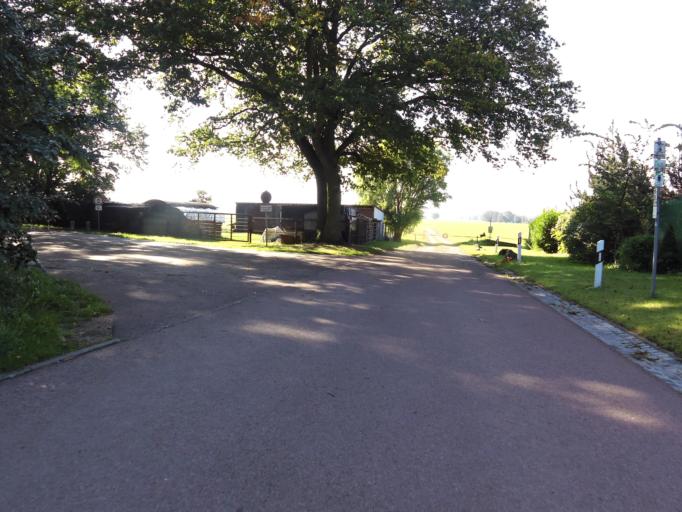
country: DE
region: Saxony-Anhalt
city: Coswig
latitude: 51.8796
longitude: 12.5099
